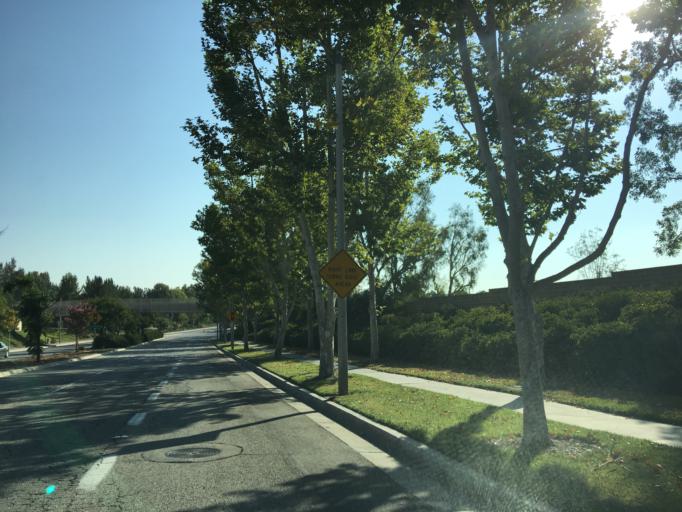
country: US
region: California
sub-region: Los Angeles County
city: Valencia
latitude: 34.4535
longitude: -118.6230
